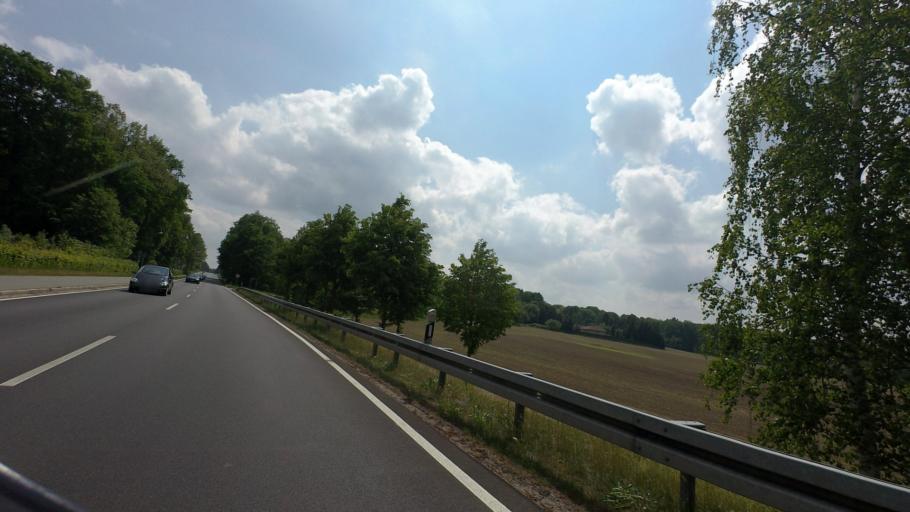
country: DE
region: Saxony
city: Rietschen
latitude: 51.3554
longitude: 14.8020
